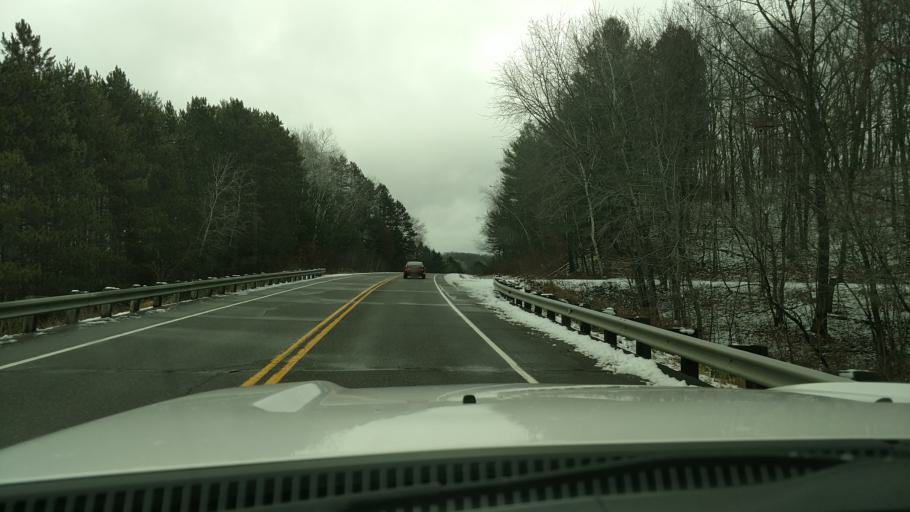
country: US
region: Wisconsin
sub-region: Dunn County
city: Boyceville
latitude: 45.1394
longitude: -91.9809
